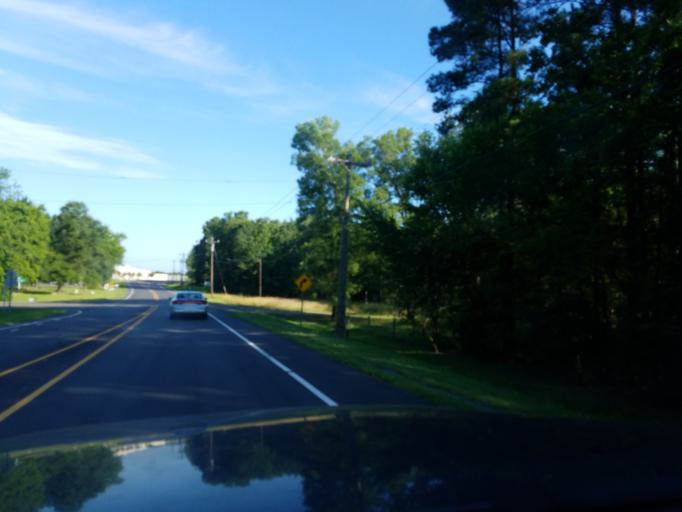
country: US
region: North Carolina
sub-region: Granville County
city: Butner
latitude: 36.1221
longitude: -78.7478
